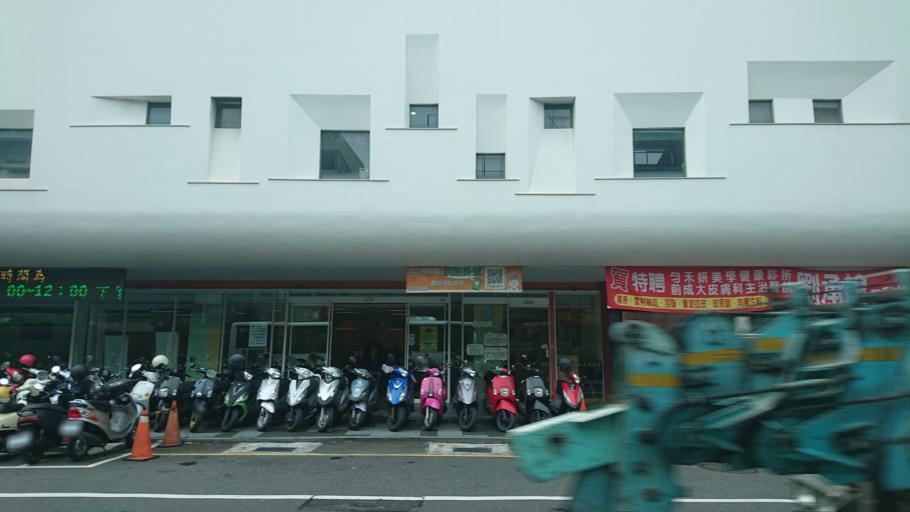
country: TW
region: Taiwan
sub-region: Tainan
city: Tainan
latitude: 23.0086
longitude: 120.2226
